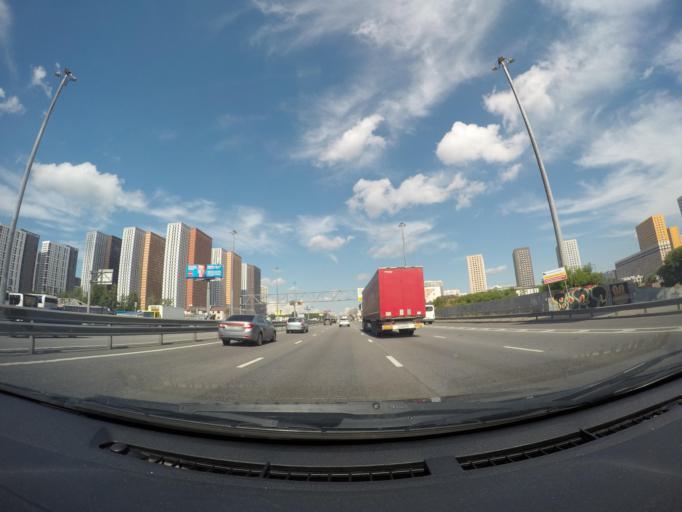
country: RU
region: Moskovskaya
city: Lyubertsy
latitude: 55.6728
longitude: 37.8637
